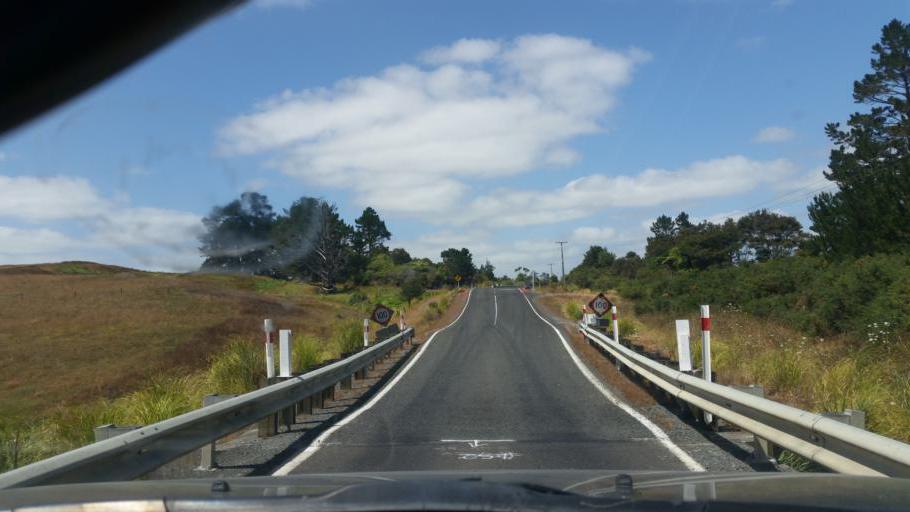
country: NZ
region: Northland
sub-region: Whangarei
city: Ruakaka
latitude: -36.0349
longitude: 174.2793
